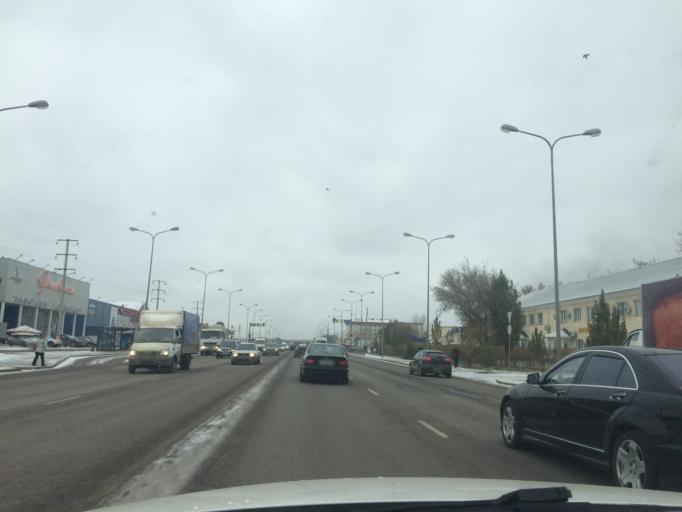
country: KZ
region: Astana Qalasy
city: Astana
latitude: 51.1823
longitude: 71.4581
